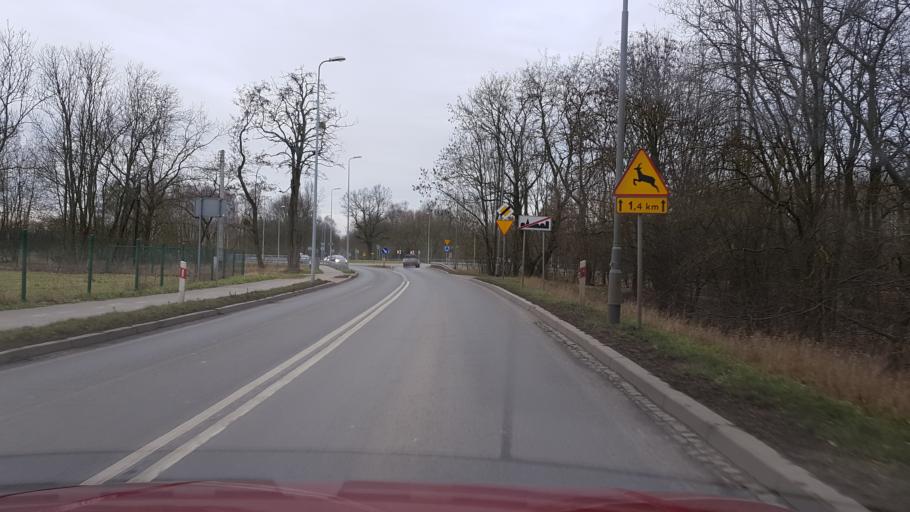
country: PL
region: West Pomeranian Voivodeship
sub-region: Powiat policki
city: Police
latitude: 53.5580
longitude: 14.5666
